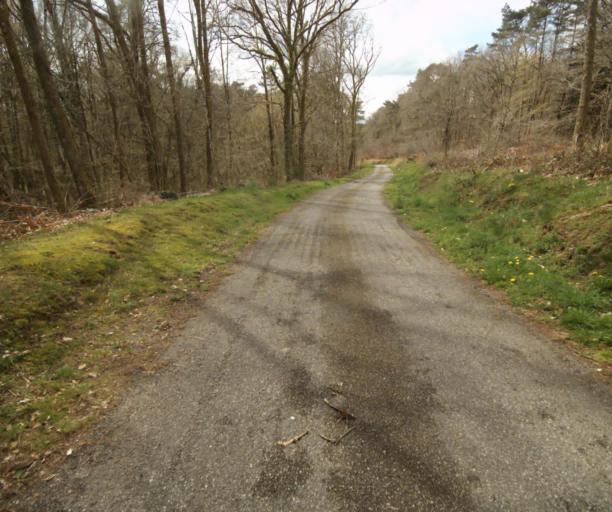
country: FR
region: Limousin
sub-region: Departement de la Correze
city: Argentat
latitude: 45.2199
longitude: 1.9178
